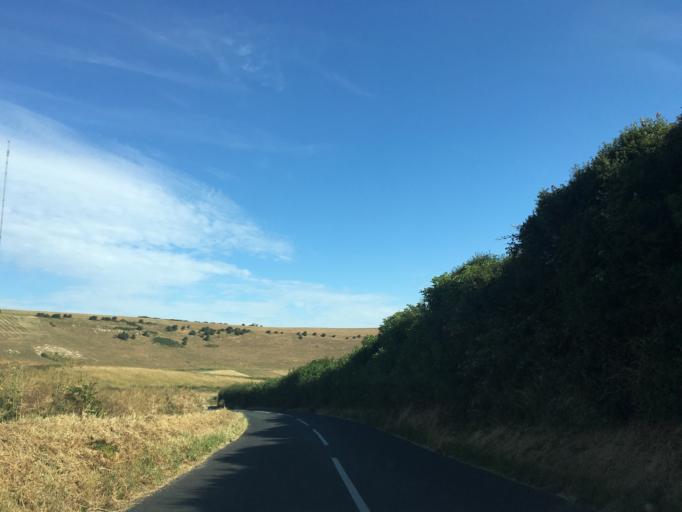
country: GB
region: England
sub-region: Isle of Wight
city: Chale
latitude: 50.6437
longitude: -1.3200
